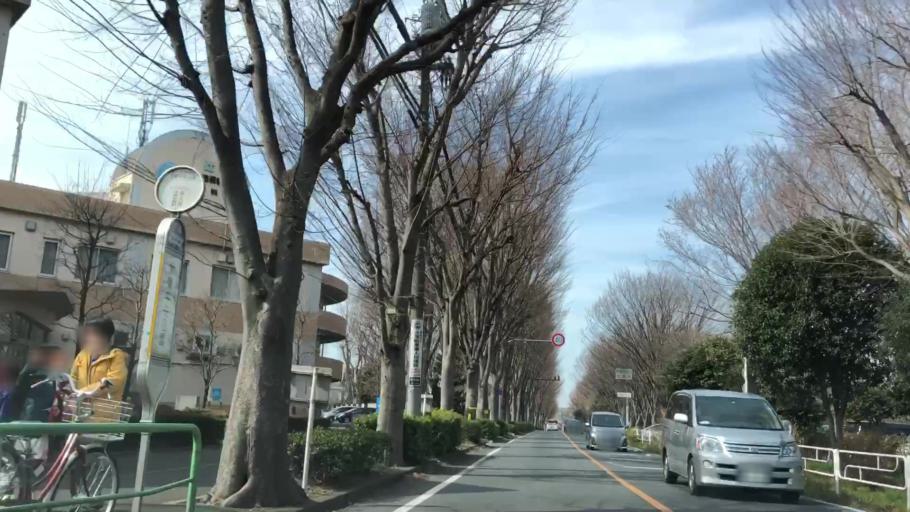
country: JP
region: Saitama
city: Wako
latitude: 35.7738
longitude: 139.5987
